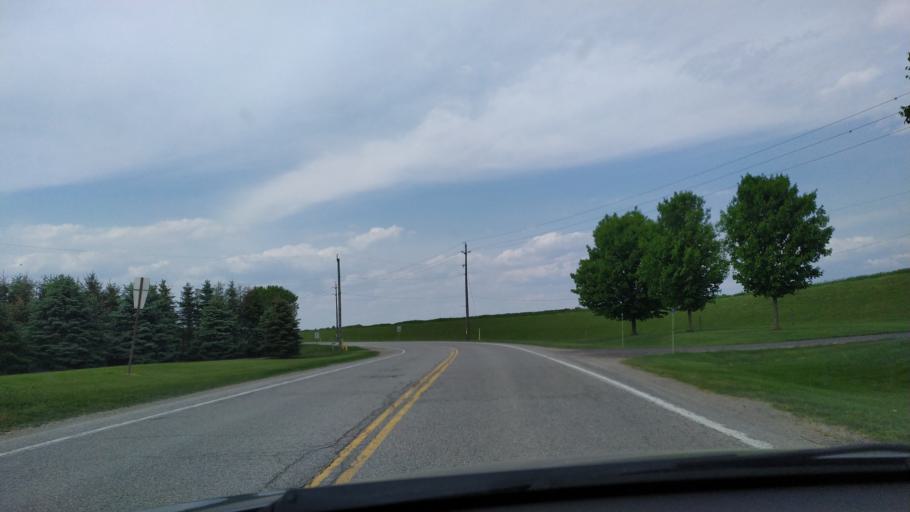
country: CA
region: Ontario
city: Ingersoll
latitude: 42.9919
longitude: -80.9553
